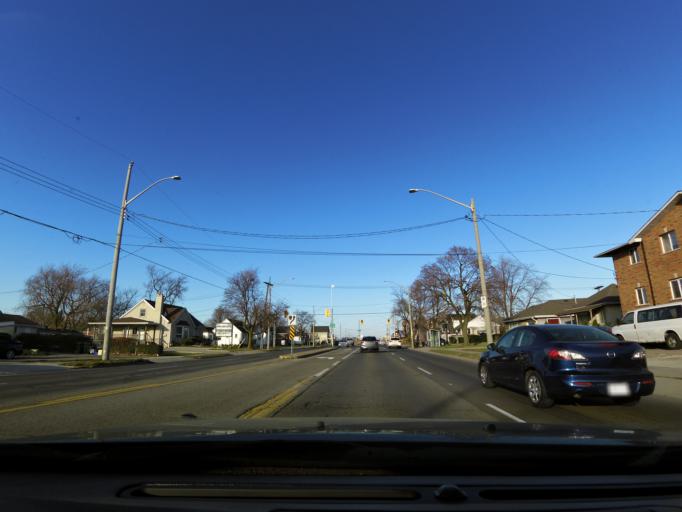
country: CA
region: Ontario
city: Hamilton
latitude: 43.2326
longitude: -79.8800
